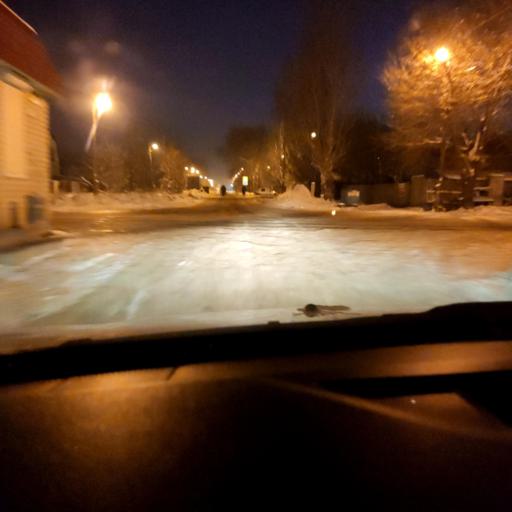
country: RU
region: Samara
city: Petra-Dubrava
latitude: 53.2458
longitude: 50.3215
